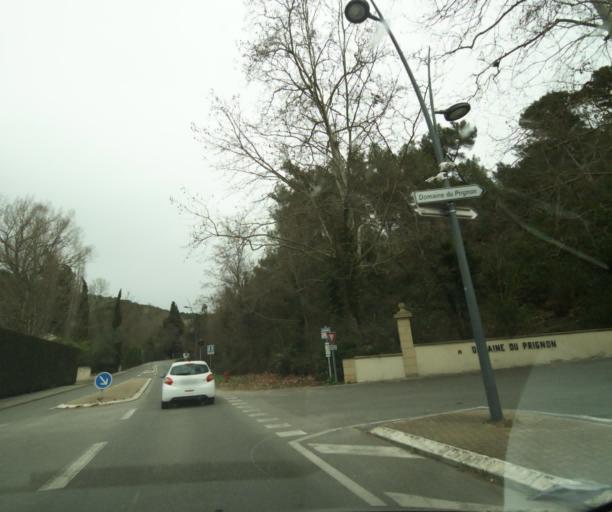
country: FR
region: Provence-Alpes-Cote d'Azur
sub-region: Departement des Bouches-du-Rhone
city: Saint-Marc-Jaumegarde
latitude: 43.5384
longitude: 5.4847
